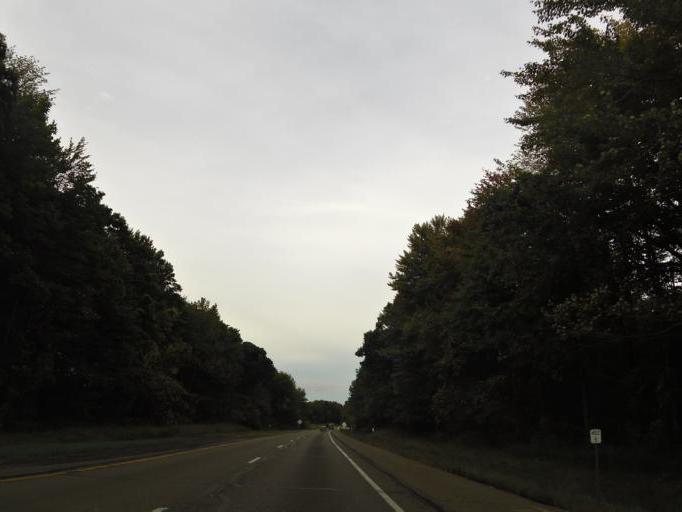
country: US
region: New York
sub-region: Erie County
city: Lake Erie Beach
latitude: 42.5818
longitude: -79.0652
